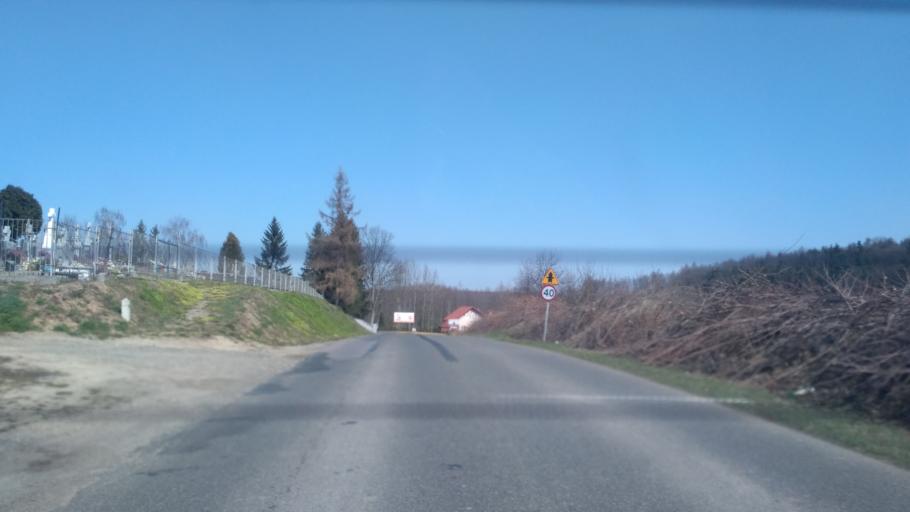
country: PL
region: Subcarpathian Voivodeship
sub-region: Powiat jaroslawski
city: Pawlosiow
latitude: 49.9595
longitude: 22.6654
